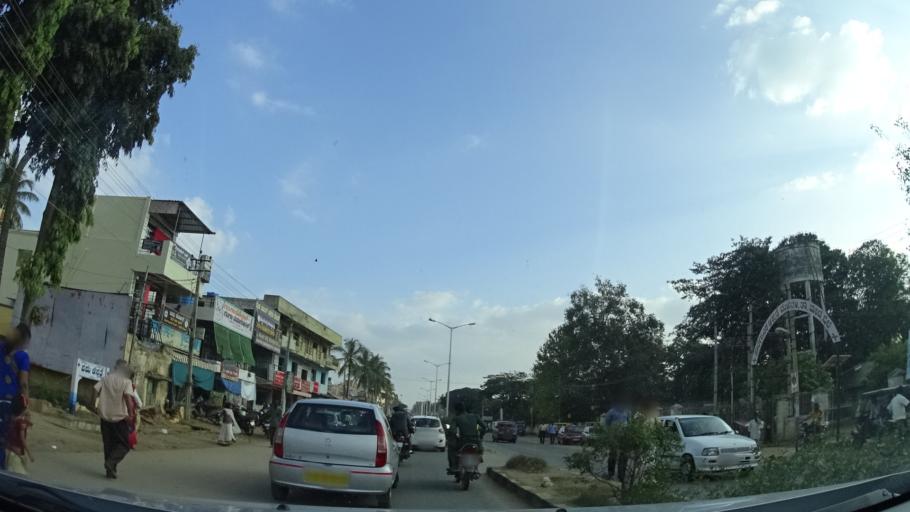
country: IN
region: Karnataka
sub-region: Mandya
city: Malavalli
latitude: 12.3849
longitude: 77.0602
